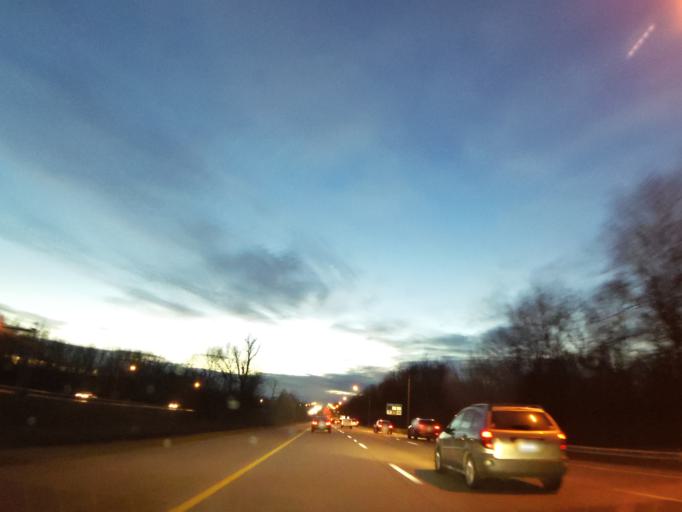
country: US
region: Kentucky
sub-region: Jefferson County
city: Middletown
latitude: 38.2233
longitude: -85.5164
